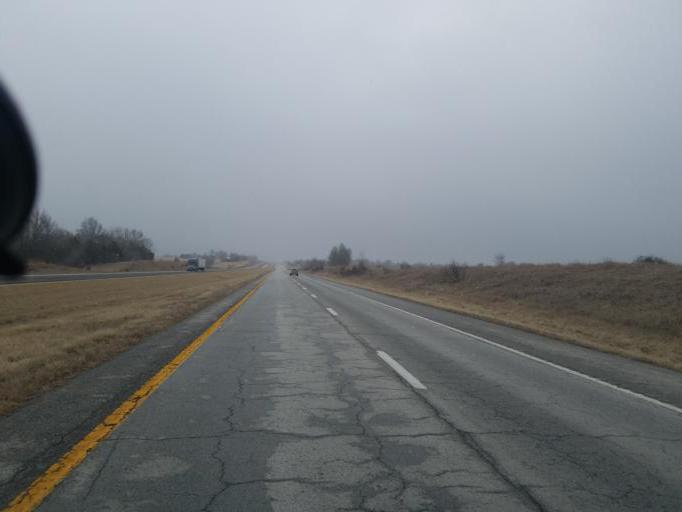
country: US
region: Missouri
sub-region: Macon County
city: La Plata
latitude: 39.9105
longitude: -92.4736
